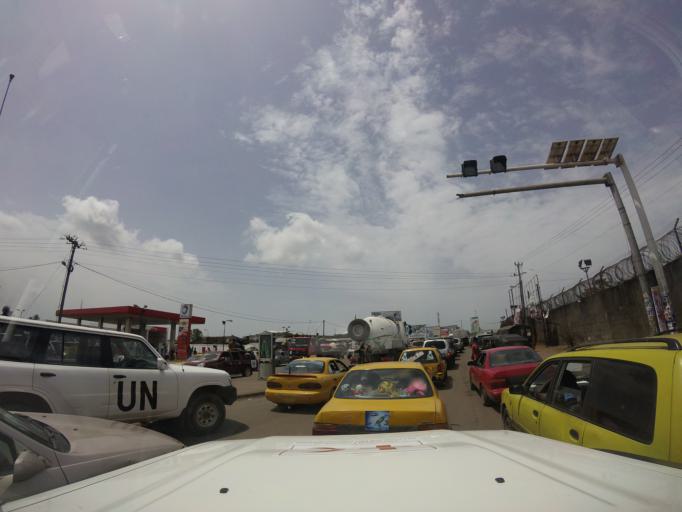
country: LR
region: Montserrado
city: Monrovia
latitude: 6.3372
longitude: -10.7936
